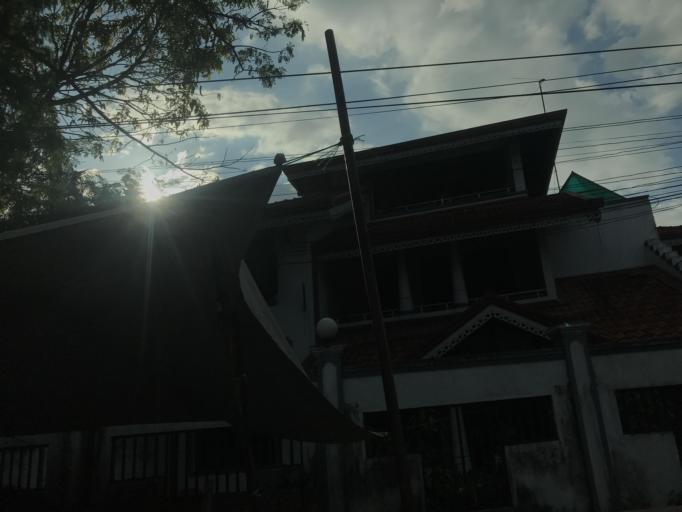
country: LK
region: Western
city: Gampaha
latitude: 7.0667
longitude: 80.0048
